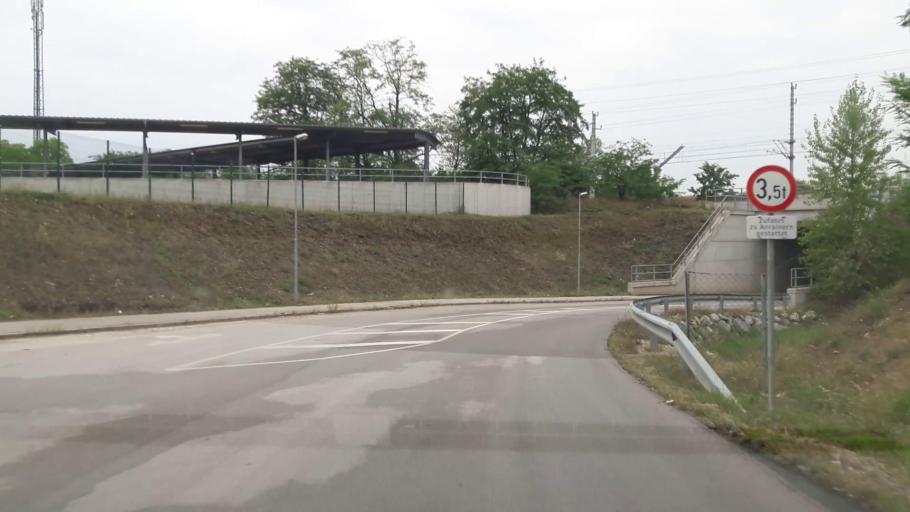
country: AT
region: Lower Austria
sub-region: Politischer Bezirk Ganserndorf
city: Strasshof an der Nordbahn
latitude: 48.3216
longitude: 16.6510
